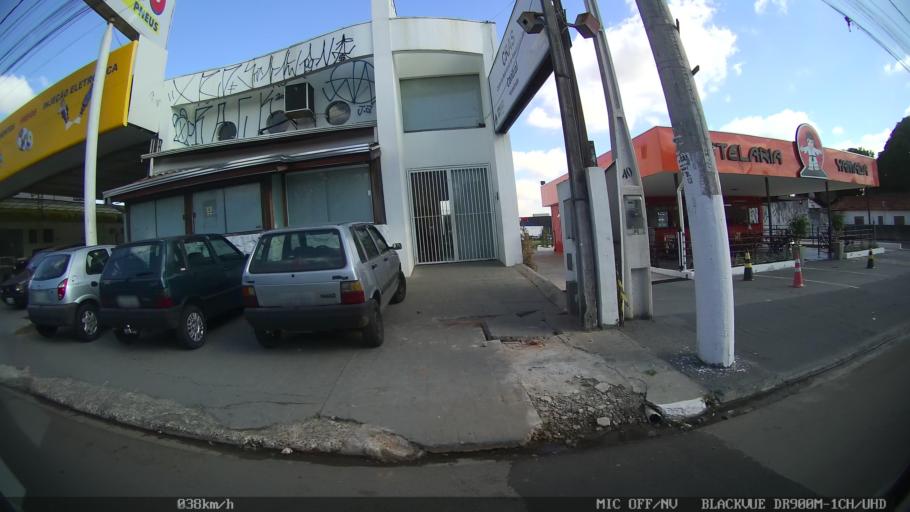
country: BR
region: Sao Paulo
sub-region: Hortolandia
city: Hortolandia
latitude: -22.8627
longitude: -47.2167
